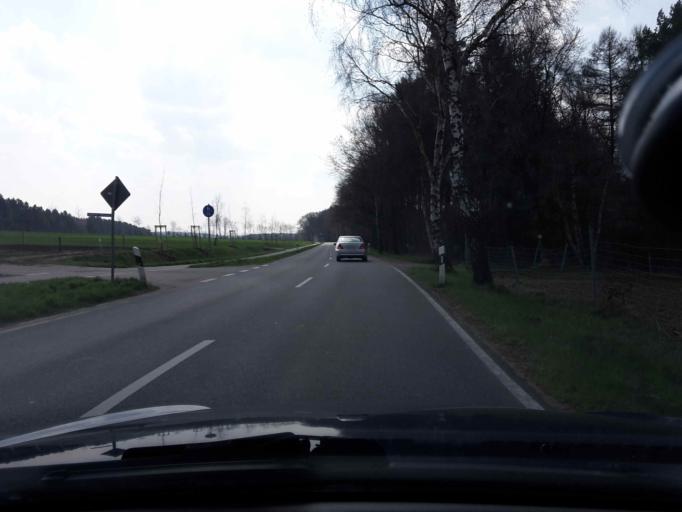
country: DE
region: Lower Saxony
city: Buchholz in der Nordheide
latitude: 53.3067
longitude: 9.9074
